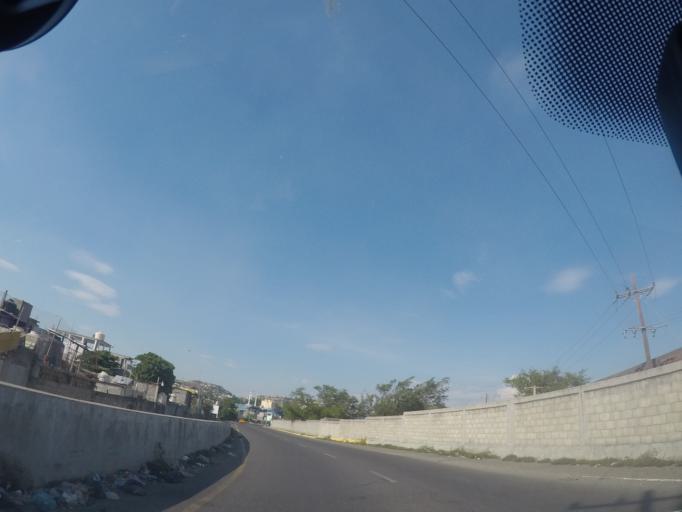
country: MX
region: Oaxaca
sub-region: Salina Cruz
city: Salina Cruz
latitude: 16.1726
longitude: -95.1986
